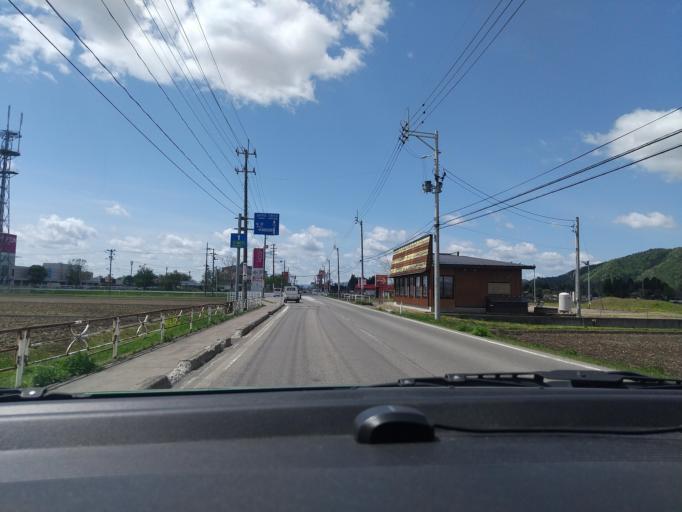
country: JP
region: Akita
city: Kakunodatemachi
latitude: 39.5542
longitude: 140.5516
